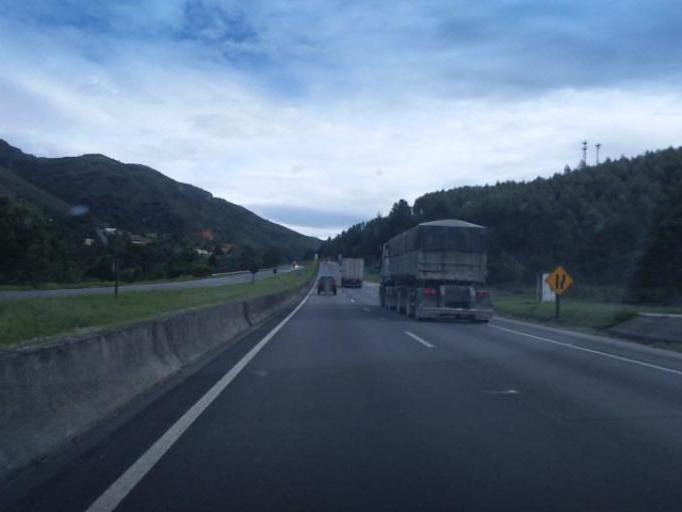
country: BR
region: Parana
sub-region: Campina Grande Do Sul
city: Campina Grande do Sul
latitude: -25.1313
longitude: -48.8574
